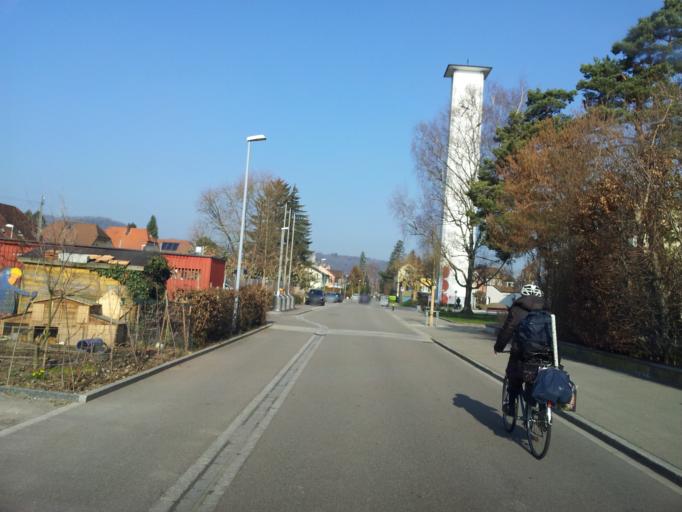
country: CH
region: Aargau
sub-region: Bezirk Baden
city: Wettingen
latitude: 47.4673
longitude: 8.3183
